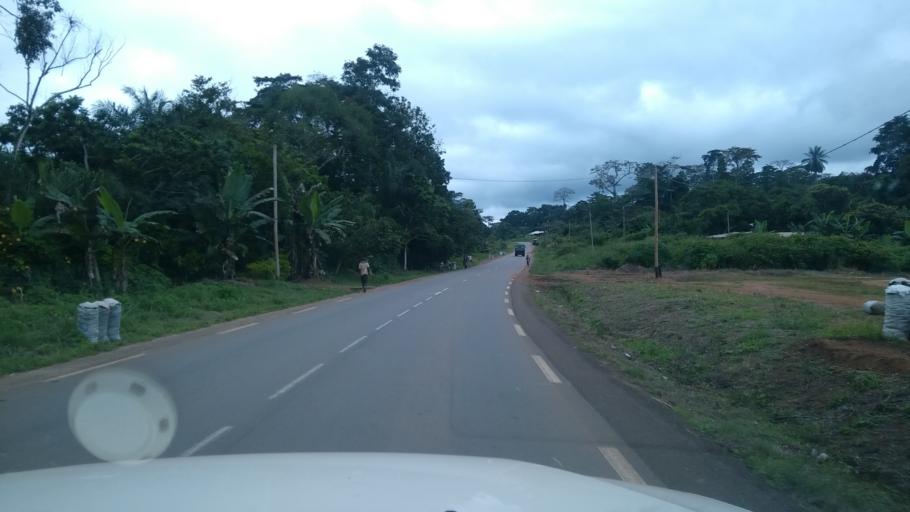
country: CM
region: Centre
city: Mbalmayo
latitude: 3.5932
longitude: 11.5190
